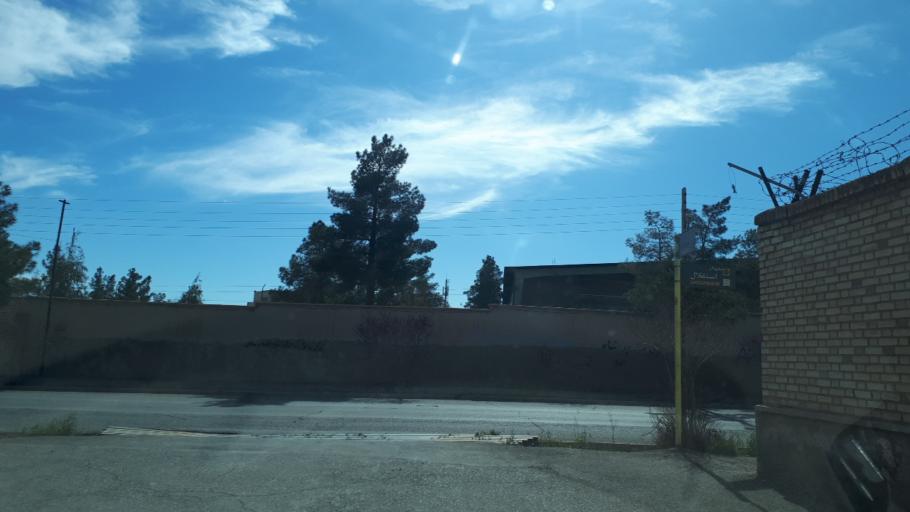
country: IR
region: Semnan
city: Semnan
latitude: 35.5844
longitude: 53.3849
